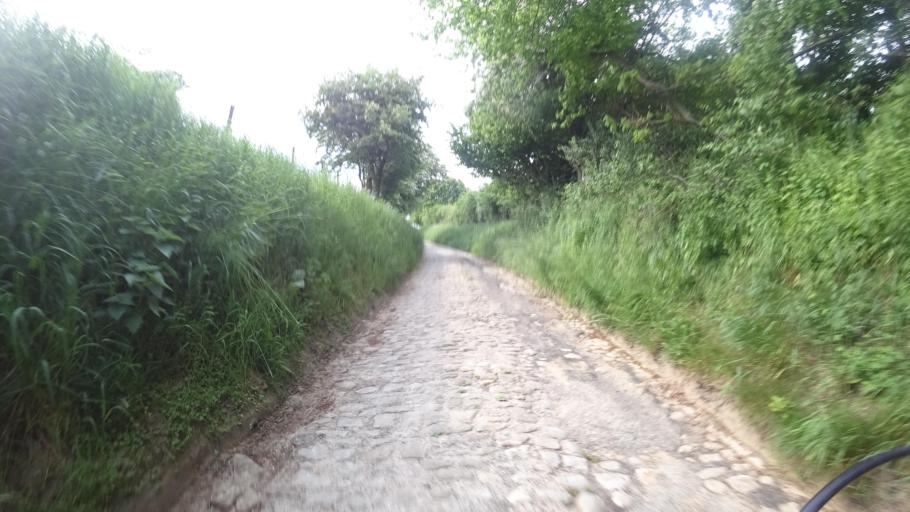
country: BE
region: Wallonia
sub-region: Province du Brabant Wallon
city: Walhain-Saint-Paul
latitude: 50.6684
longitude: 4.6686
